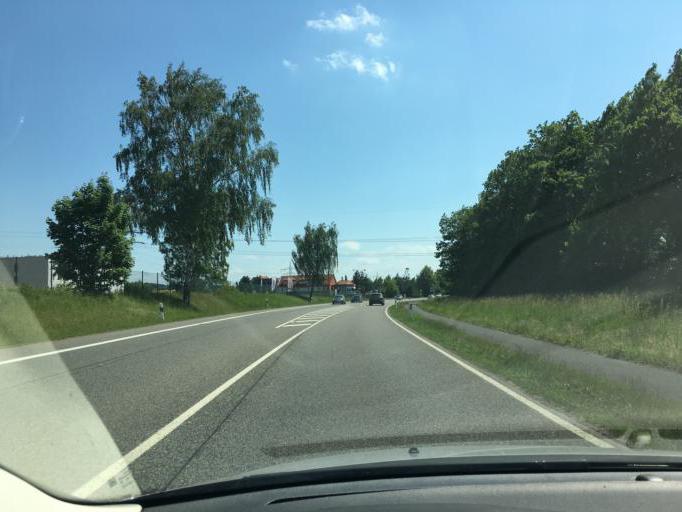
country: DE
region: Hesse
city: Bebra
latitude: 50.9854
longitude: 9.7814
